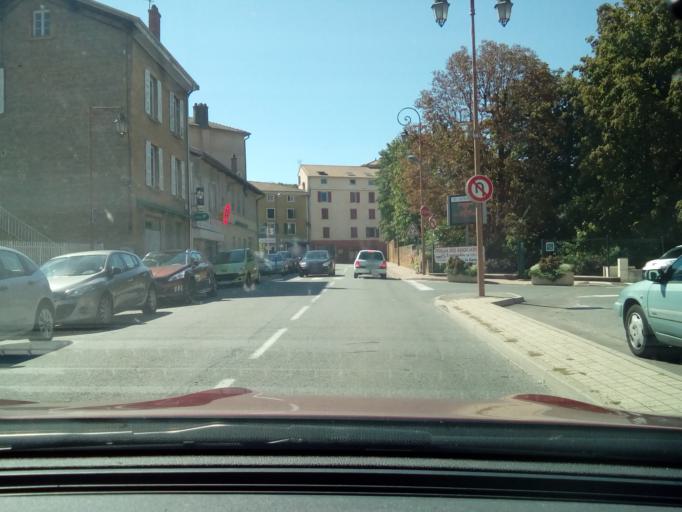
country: FR
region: Rhone-Alpes
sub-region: Departement du Rhone
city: Lozanne
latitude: 45.8550
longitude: 4.6813
